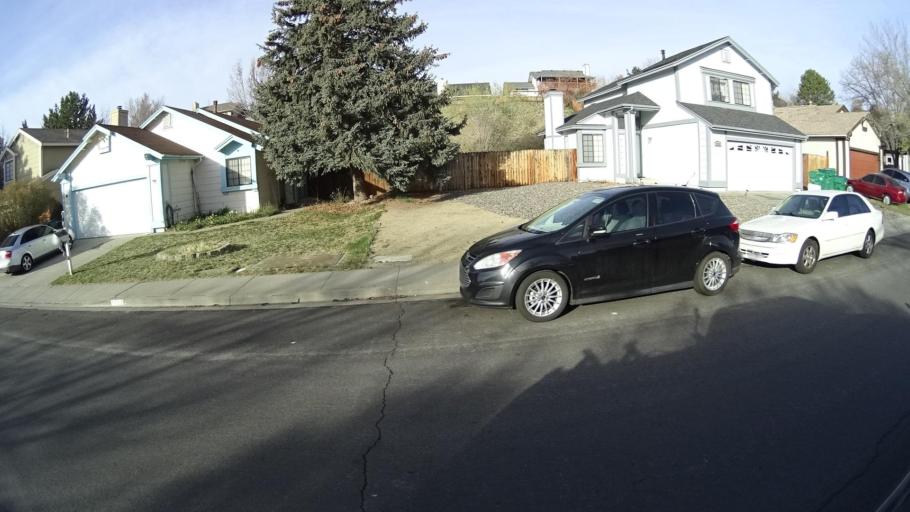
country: US
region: Nevada
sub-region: Washoe County
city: Reno
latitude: 39.5299
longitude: -119.8682
